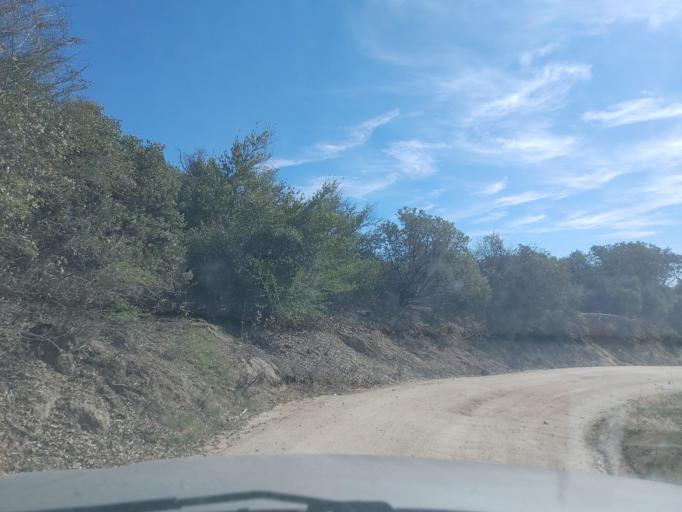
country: US
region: California
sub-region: Madera County
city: Ahwahnee
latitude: 37.4111
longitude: -119.6999
